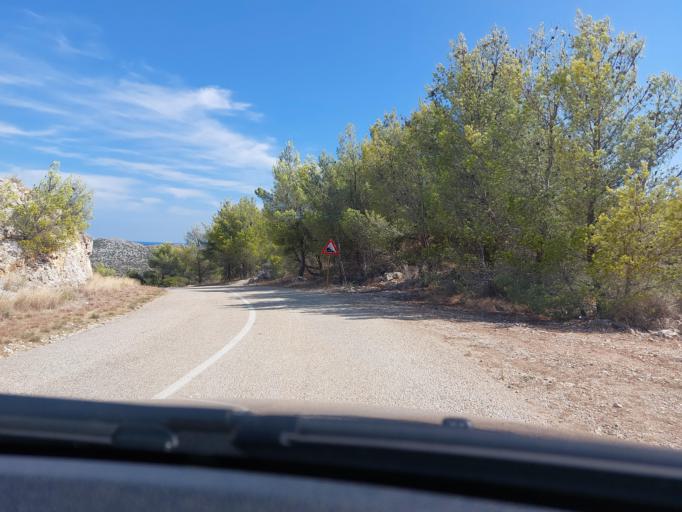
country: HR
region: Dubrovacko-Neretvanska
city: Smokvica
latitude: 42.7444
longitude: 16.8733
